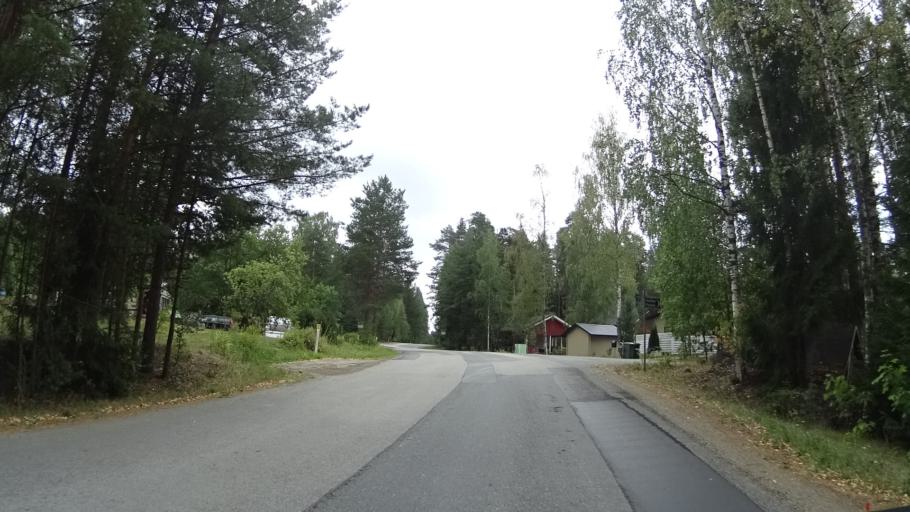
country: FI
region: Pirkanmaa
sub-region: Tampere
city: Kangasala
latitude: 61.4515
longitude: 24.1170
